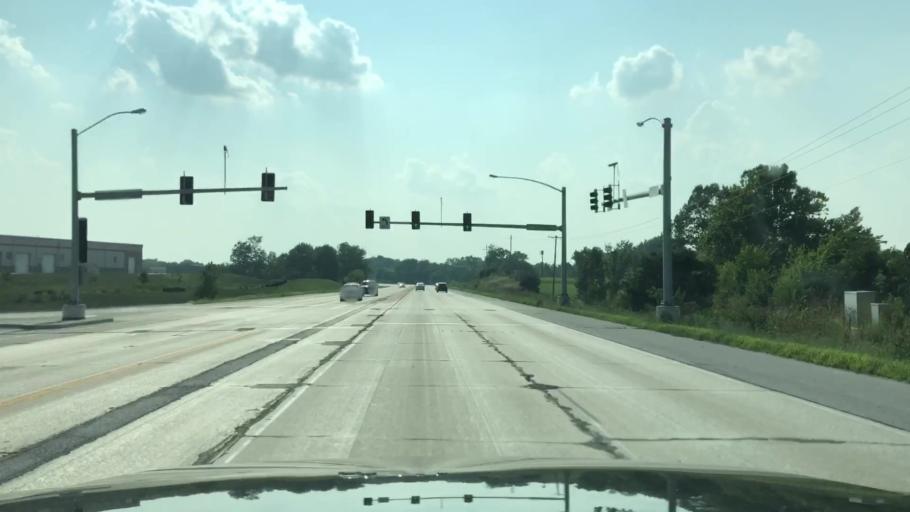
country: US
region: Missouri
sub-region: Saint Charles County
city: Wentzville
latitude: 38.8268
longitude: -90.8396
